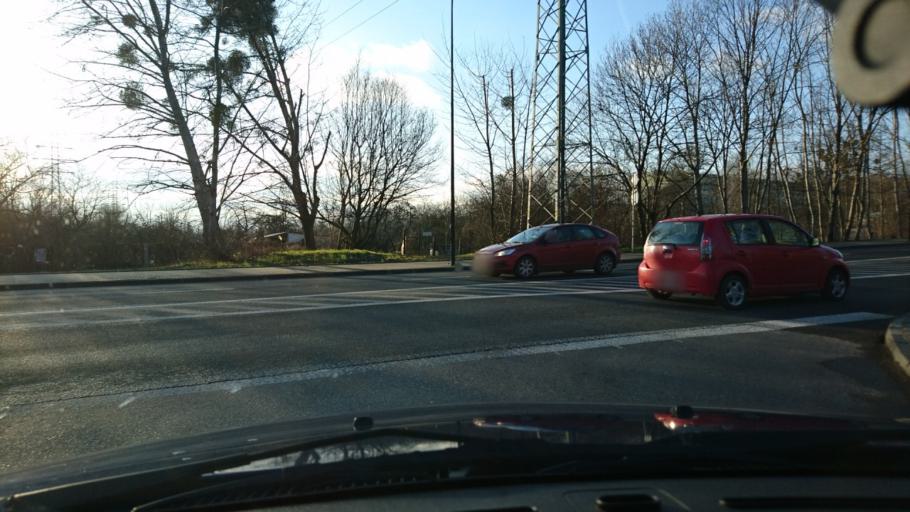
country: PL
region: Silesian Voivodeship
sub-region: Gliwice
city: Gliwice
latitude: 50.3154
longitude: 18.6668
